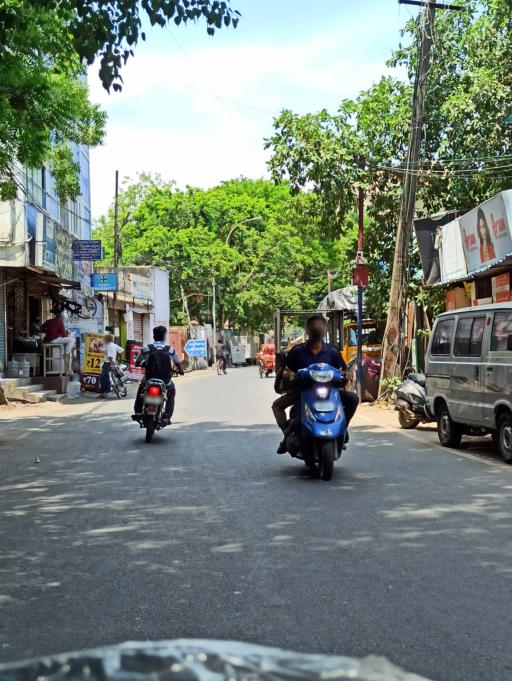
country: IN
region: Tamil Nadu
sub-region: Chennai
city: Chetput
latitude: 13.0582
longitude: 80.2299
